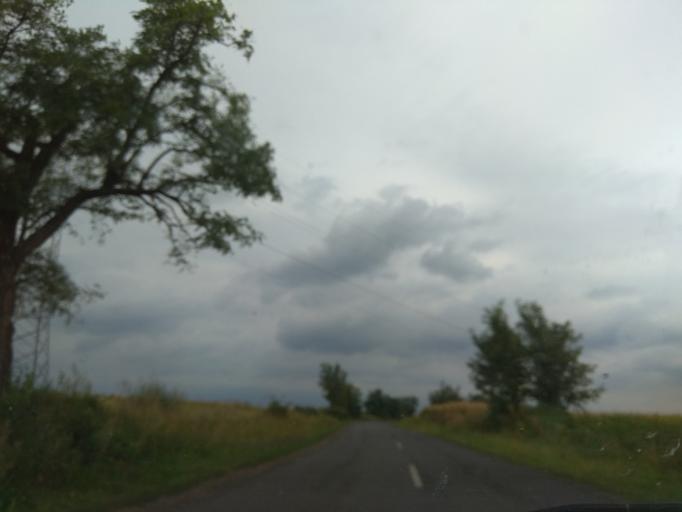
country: HU
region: Borsod-Abauj-Zemplen
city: Gesztely
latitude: 48.1247
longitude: 20.9728
